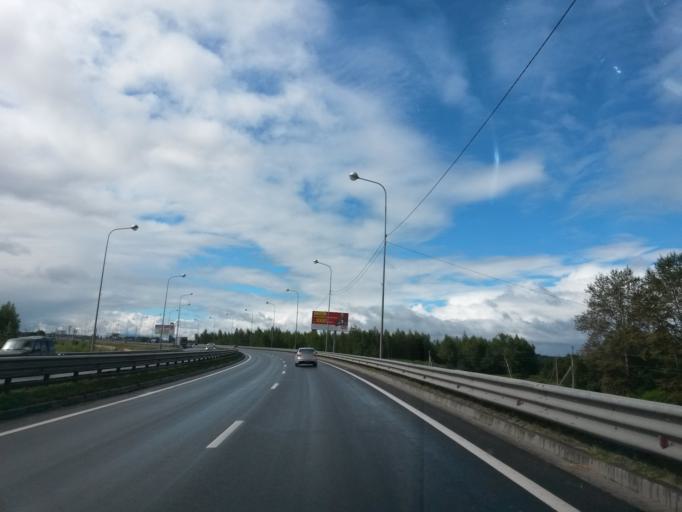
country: RU
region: Jaroslavl
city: Yaroslavl
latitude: 57.6838
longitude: 39.8773
